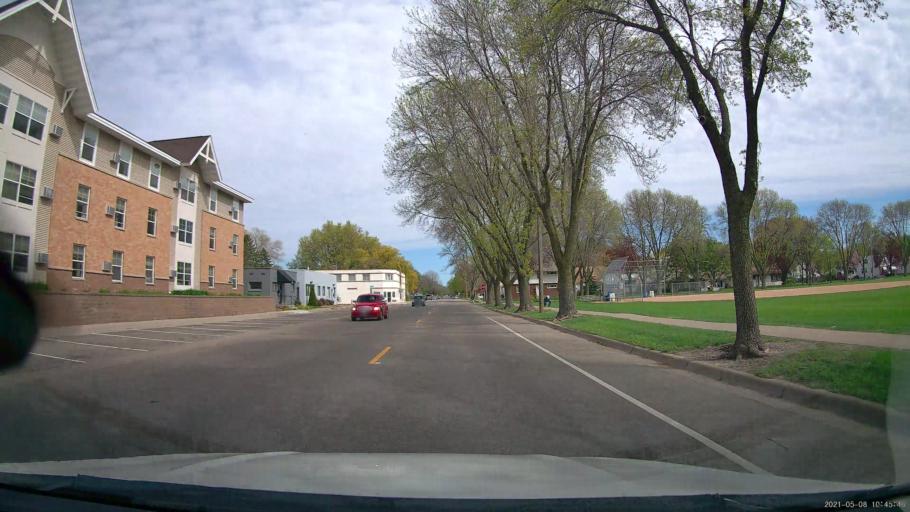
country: US
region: Minnesota
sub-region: Dakota County
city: South Saint Paul
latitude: 44.8954
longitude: -93.0526
